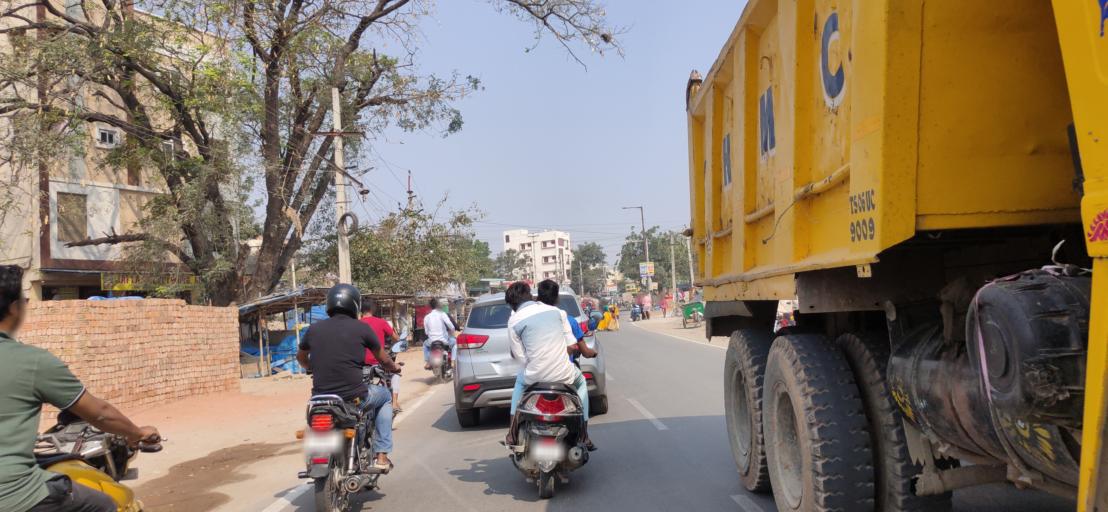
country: IN
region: Telangana
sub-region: Rangareddi
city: Kukatpalli
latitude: 17.5029
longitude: 78.4081
